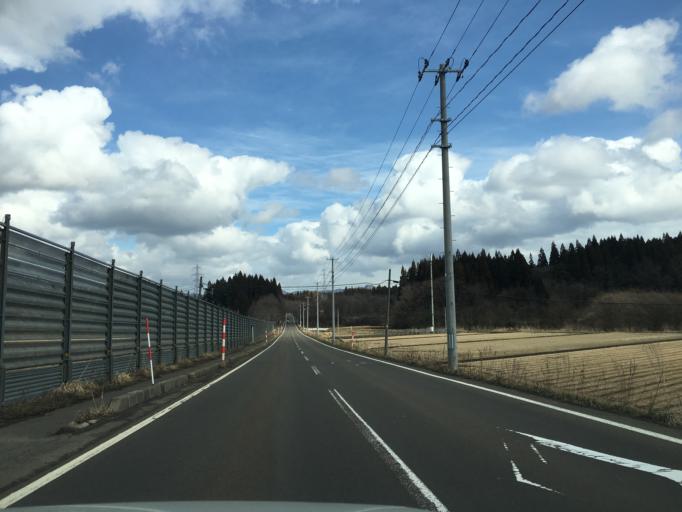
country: JP
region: Akita
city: Odate
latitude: 40.1991
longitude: 140.5356
